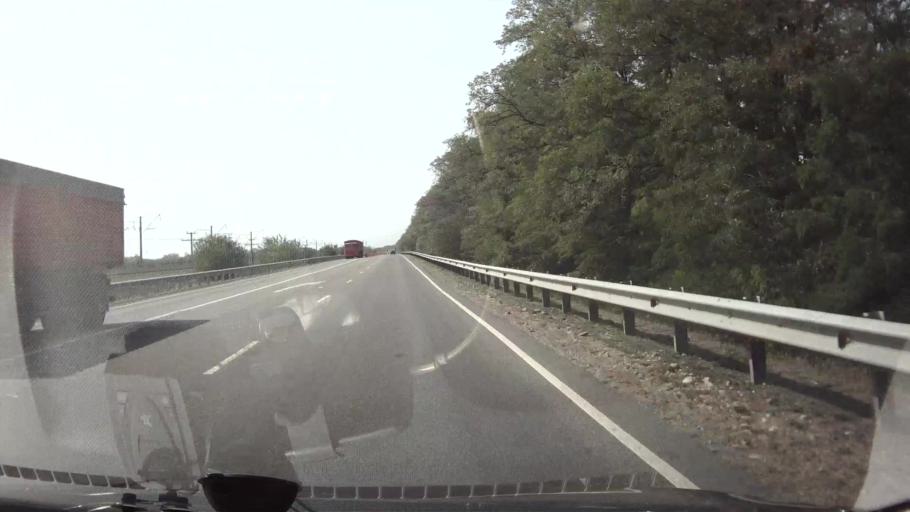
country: RU
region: Krasnodarskiy
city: Dvubratskiy
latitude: 45.2788
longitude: 39.8346
